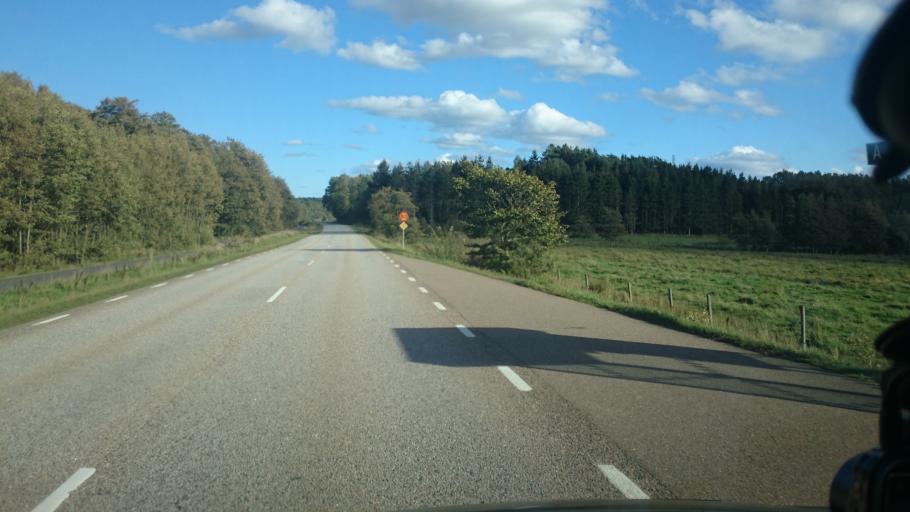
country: SE
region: Vaestra Goetaland
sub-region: Lysekils Kommun
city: Brastad
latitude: 58.3314
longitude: 11.4575
